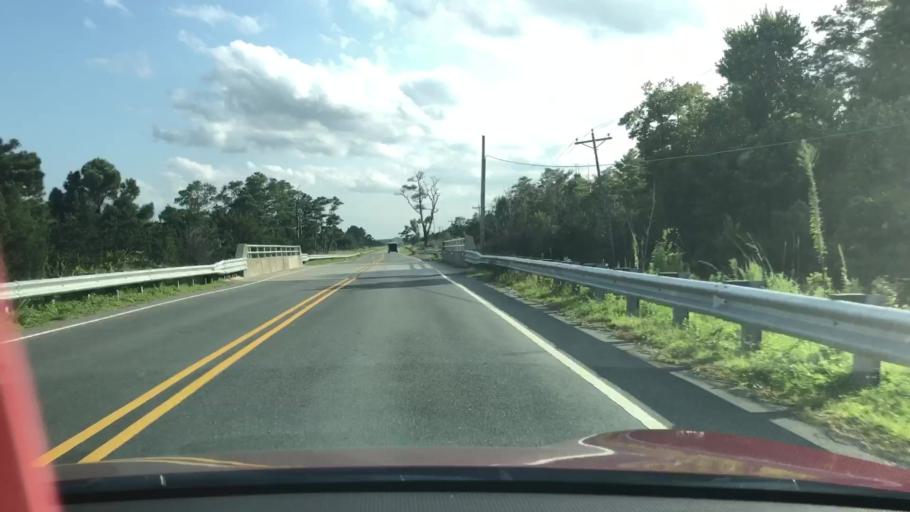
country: US
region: North Carolina
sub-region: Dare County
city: Wanchese
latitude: 35.7063
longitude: -75.7687
